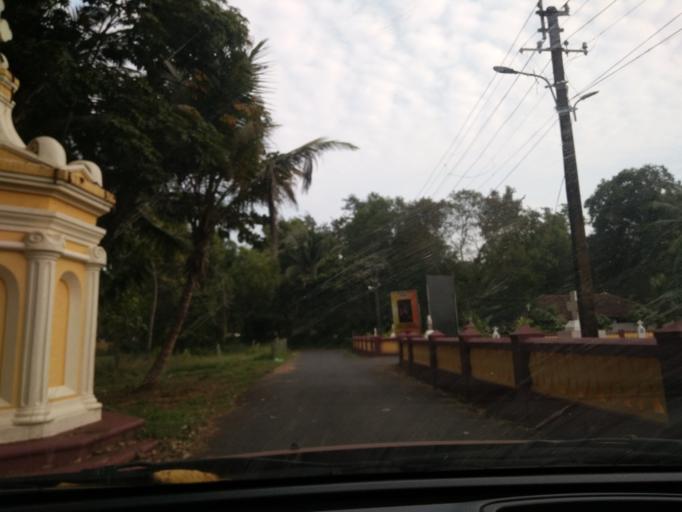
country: IN
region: Goa
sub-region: South Goa
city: Varca
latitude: 15.2208
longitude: 73.9568
